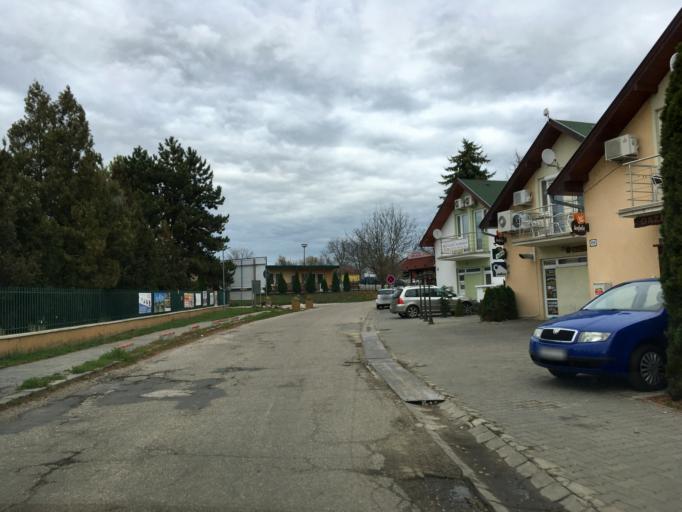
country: SK
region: Nitriansky
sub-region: Okres Nitra
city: Vrable
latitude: 48.0995
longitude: 18.3372
